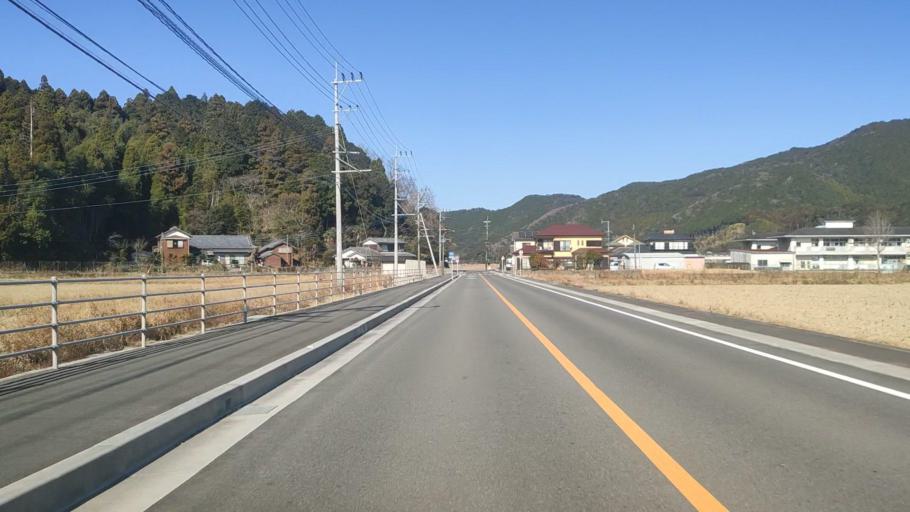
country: JP
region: Oita
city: Saiki
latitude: 32.9223
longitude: 131.9267
